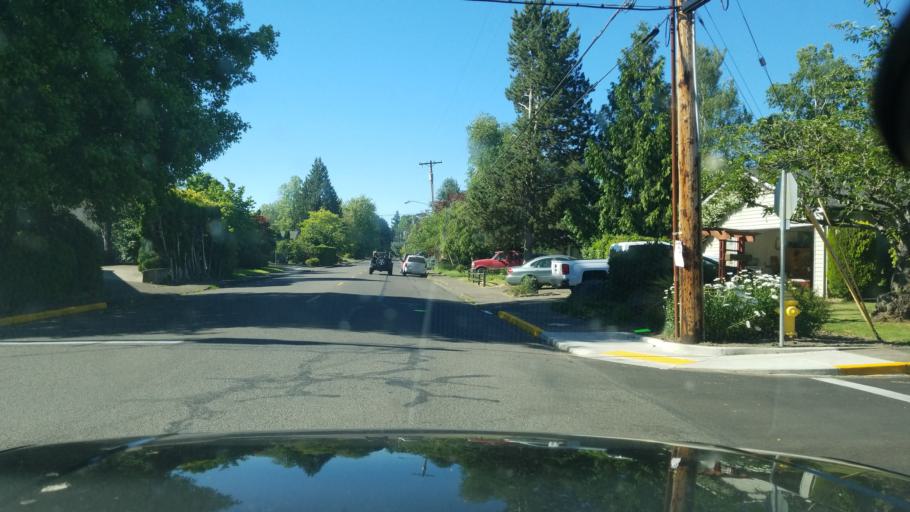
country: US
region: Oregon
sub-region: Yamhill County
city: McMinnville
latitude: 45.2219
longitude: -123.2076
